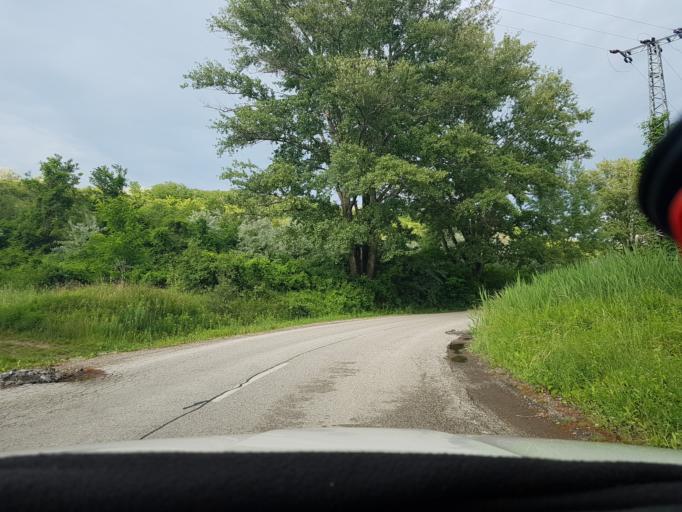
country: HU
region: Komarom-Esztergom
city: Labatlan
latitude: 47.7388
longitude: 18.5186
